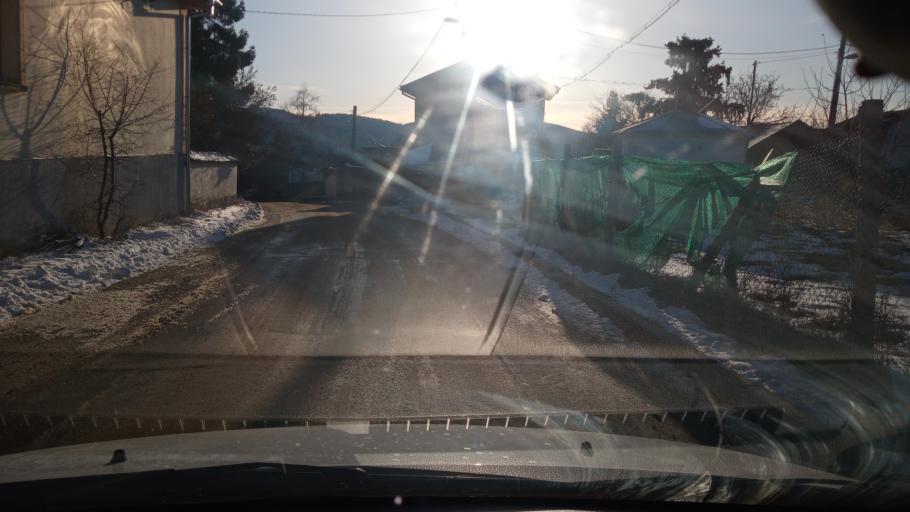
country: BG
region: Sofiya
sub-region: Obshtina Samokov
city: Samokov
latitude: 42.4802
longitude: 23.4136
